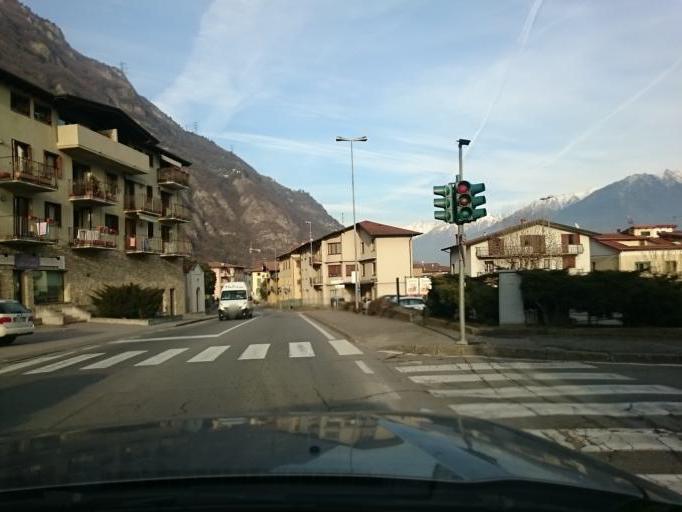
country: IT
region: Lombardy
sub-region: Provincia di Brescia
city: Piamborno
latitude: 45.9166
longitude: 10.2190
